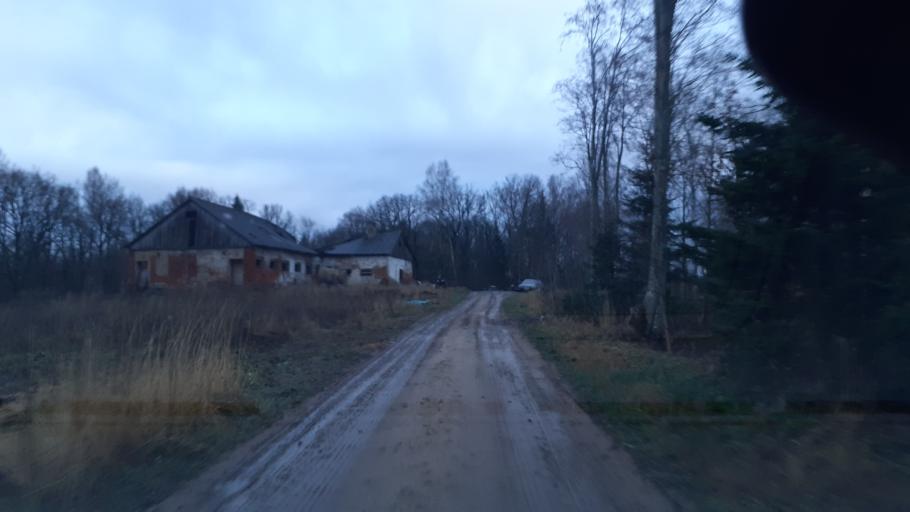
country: LV
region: Alsunga
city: Alsunga
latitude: 56.9070
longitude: 21.6965
